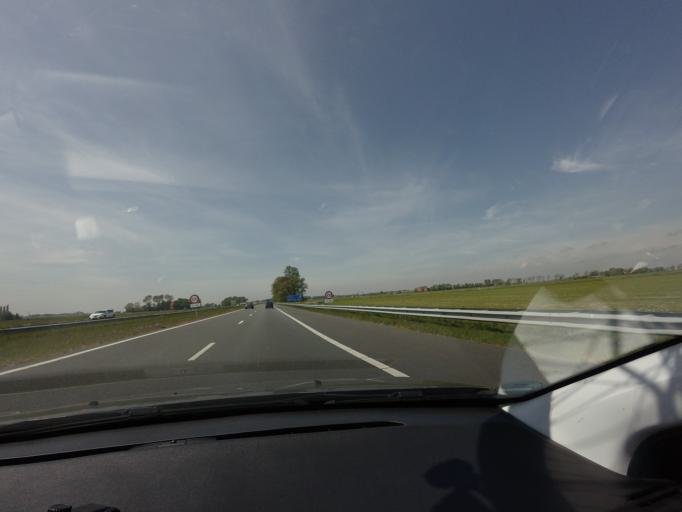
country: NL
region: Friesland
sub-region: Sudwest Fryslan
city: Bolsward
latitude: 53.0500
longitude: 5.5620
